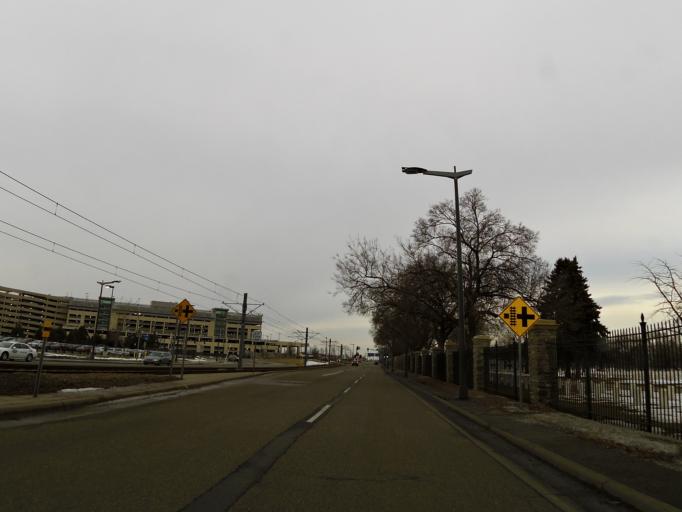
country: US
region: Minnesota
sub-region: Hennepin County
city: Richfield
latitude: 44.8709
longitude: -93.2231
